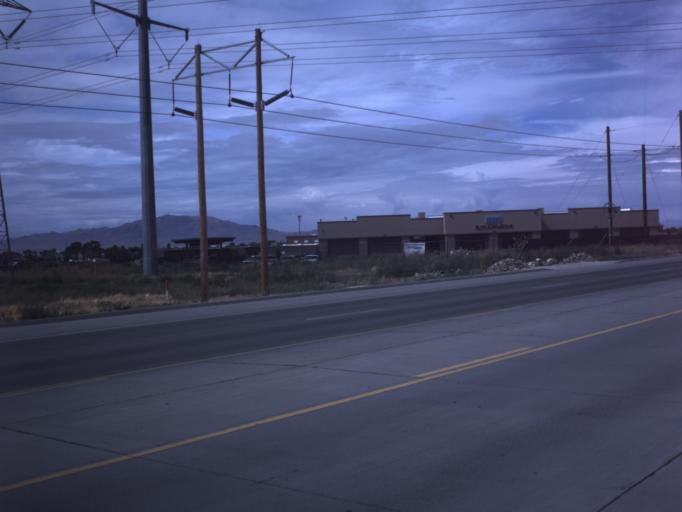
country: US
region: Utah
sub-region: Davis County
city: Syracuse
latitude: 41.1107
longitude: -112.0521
